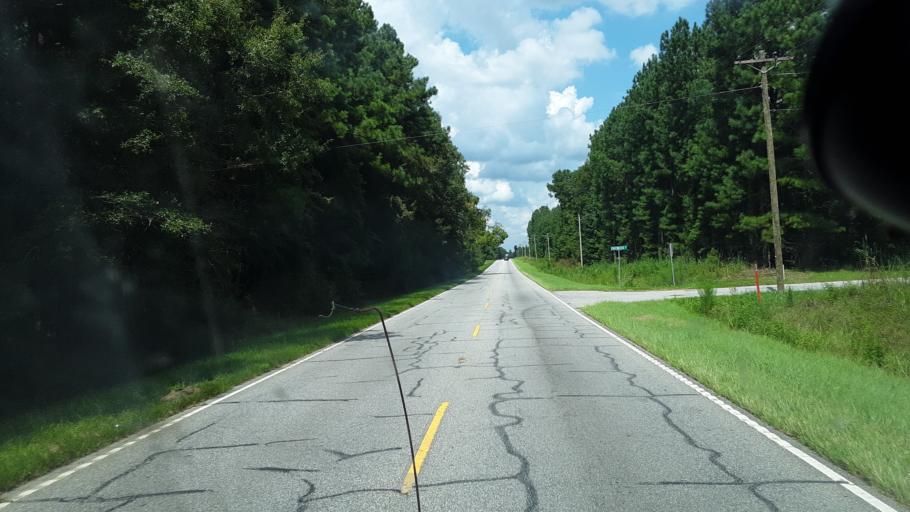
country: US
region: South Carolina
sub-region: Williamsburg County
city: Andrews
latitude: 33.6050
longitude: -79.4394
